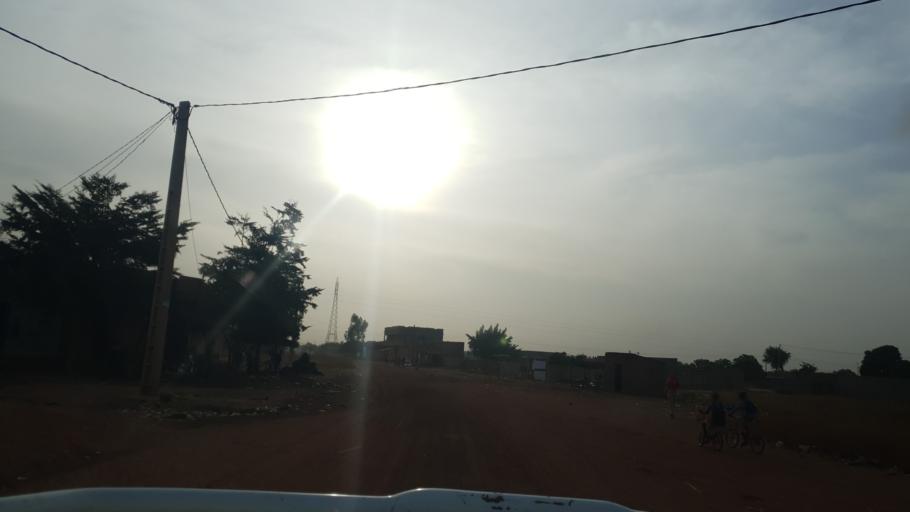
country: ML
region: Segou
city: Baroueli
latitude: 12.7759
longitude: -6.9421
